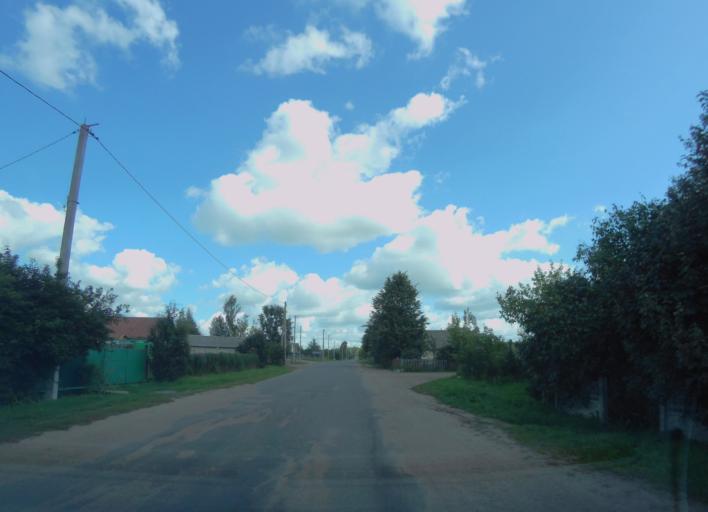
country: BY
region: Minsk
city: Zyembin
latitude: 54.3776
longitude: 28.3837
